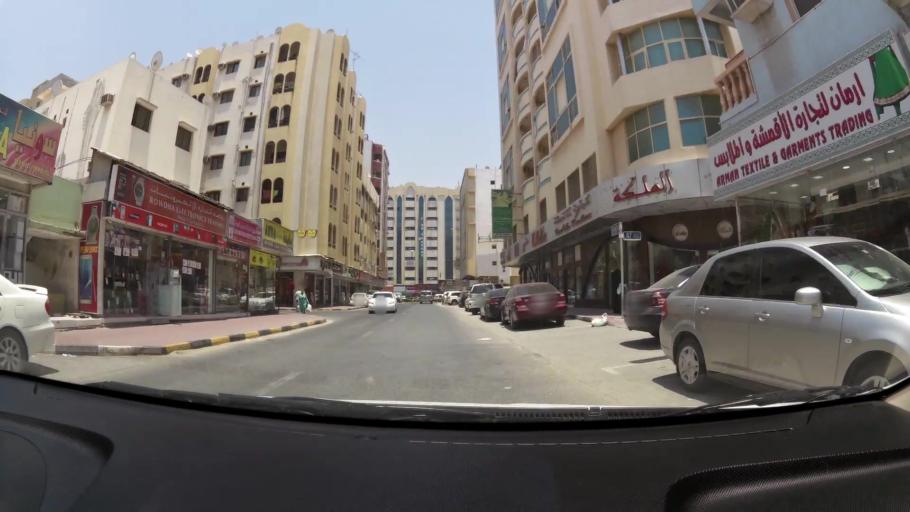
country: AE
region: Ajman
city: Ajman
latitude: 25.4111
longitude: 55.4426
